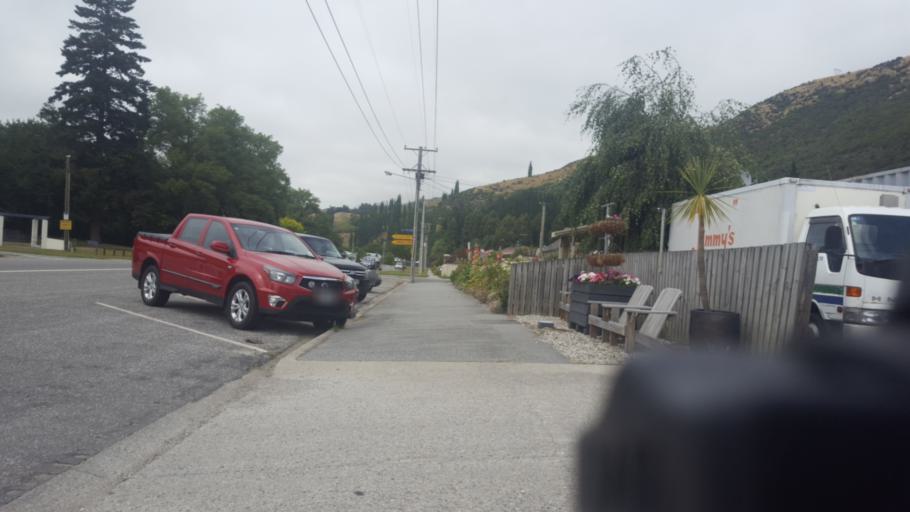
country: NZ
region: Otago
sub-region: Queenstown-Lakes District
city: Kingston
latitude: -45.5437
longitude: 169.3142
